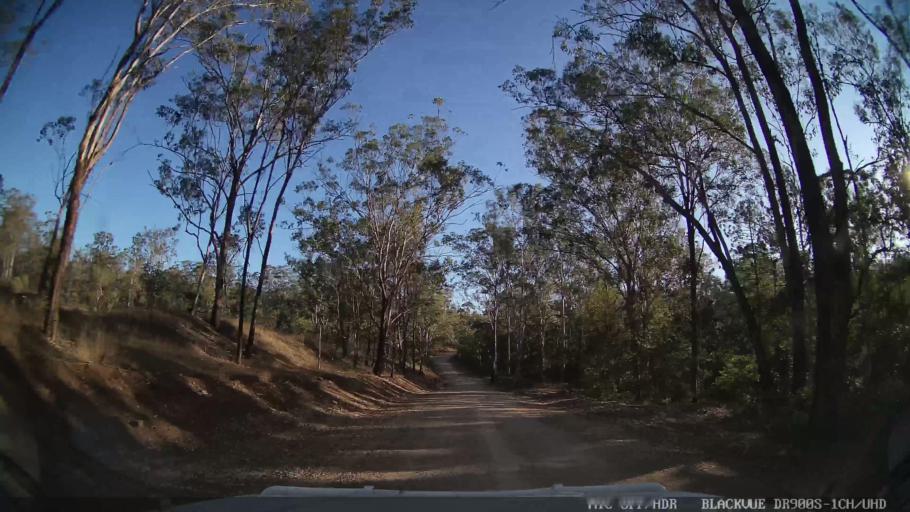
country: AU
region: Queensland
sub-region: Gladstone
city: Toolooa
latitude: -24.6833
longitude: 151.3307
